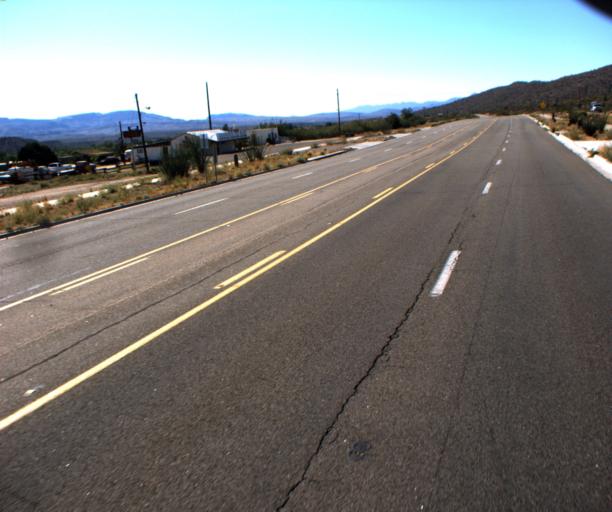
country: US
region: Arizona
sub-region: Yavapai County
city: Bagdad
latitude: 34.7012
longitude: -113.6103
